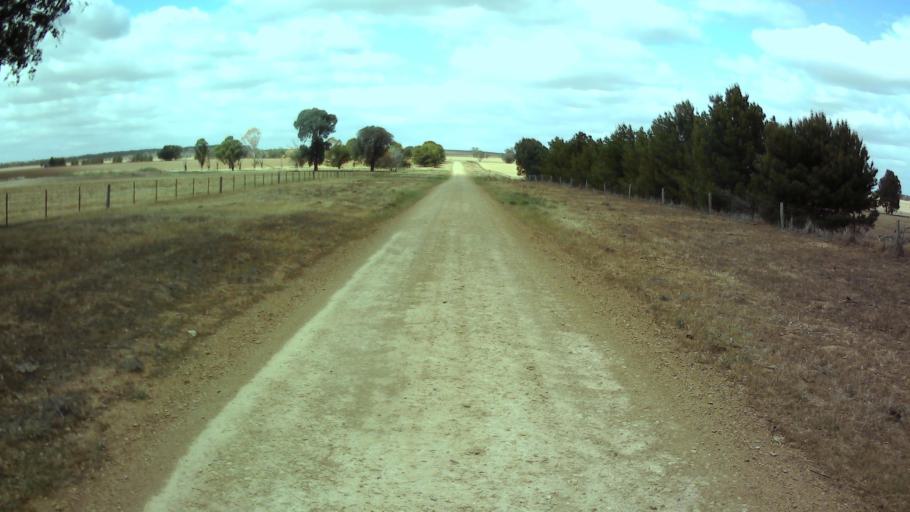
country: AU
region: New South Wales
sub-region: Weddin
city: Grenfell
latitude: -34.0610
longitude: 148.3301
